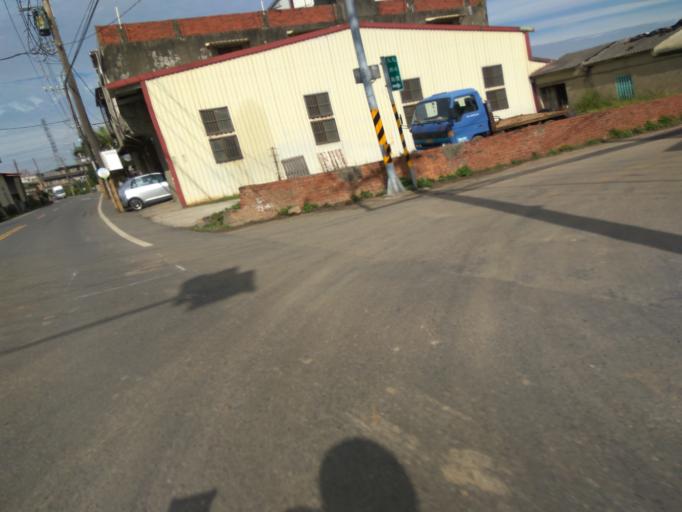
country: TW
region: Taiwan
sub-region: Hsinchu
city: Zhubei
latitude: 24.9534
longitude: 121.1275
